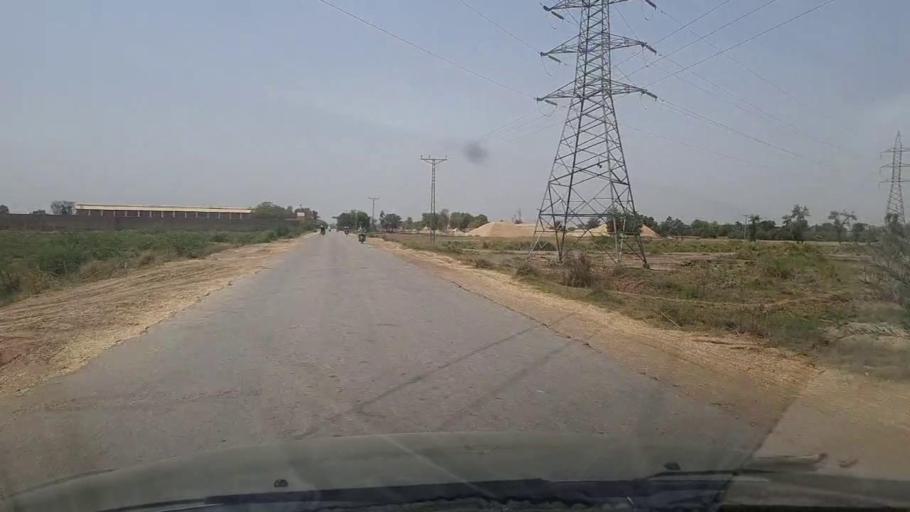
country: PK
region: Sindh
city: Karaundi
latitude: 26.8794
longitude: 68.3138
